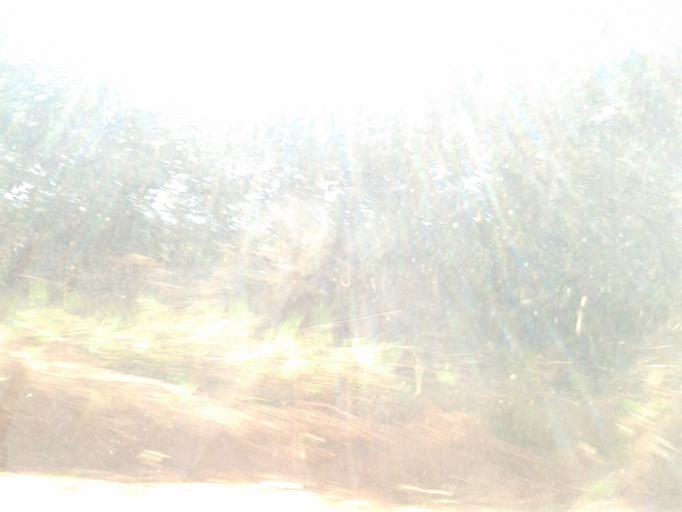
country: BR
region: Minas Gerais
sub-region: Ituiutaba
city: Ituiutaba
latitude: -19.0468
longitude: -49.3672
